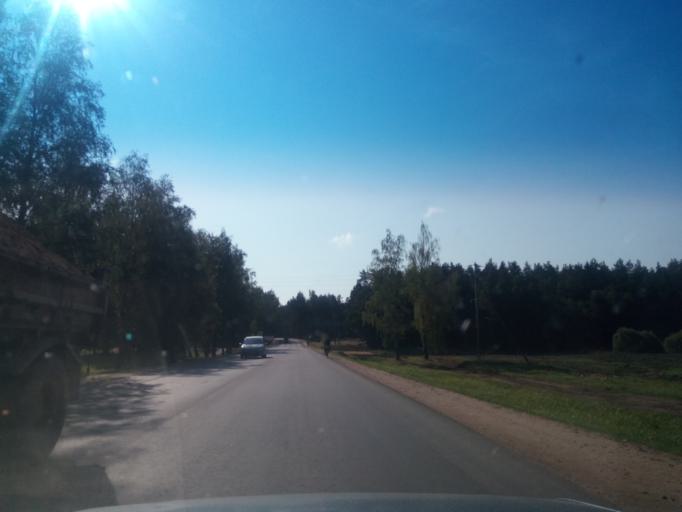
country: BY
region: Vitebsk
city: Vyerkhnyadzvinsk
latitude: 55.7619
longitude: 27.9431
